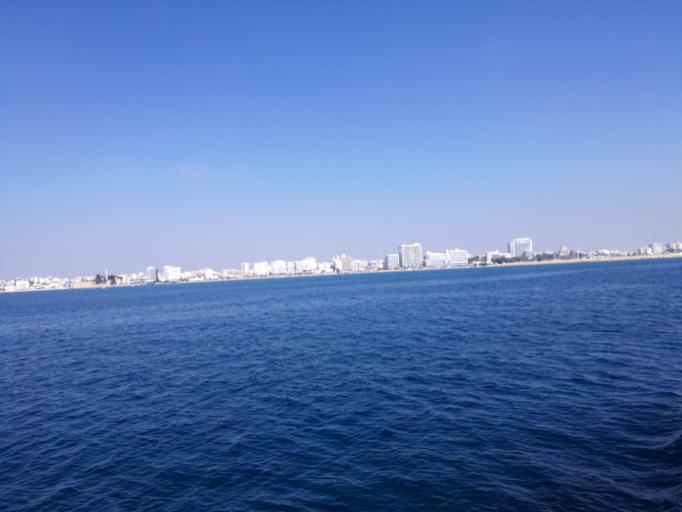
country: CY
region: Larnaka
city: Larnaca
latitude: 34.9116
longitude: 33.6480
